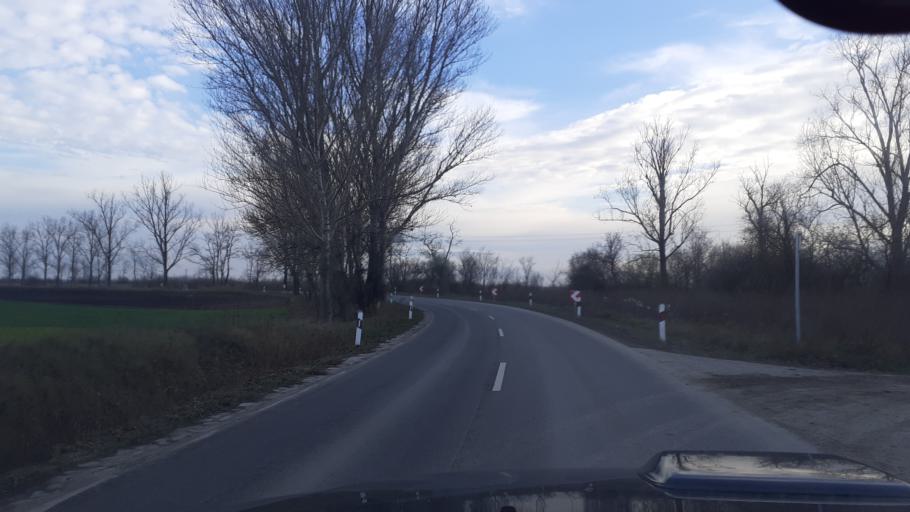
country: HU
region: Bacs-Kiskun
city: Kunszentmiklos
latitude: 47.0013
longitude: 19.1291
